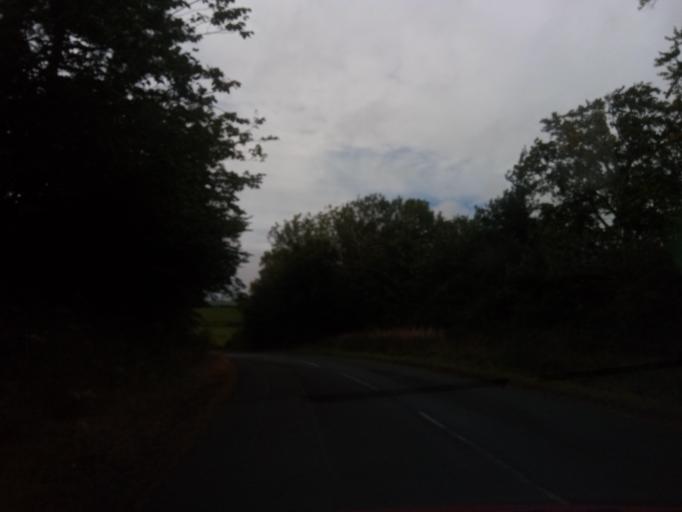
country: GB
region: Scotland
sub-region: The Scottish Borders
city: Duns
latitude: 55.7480
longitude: -2.3262
